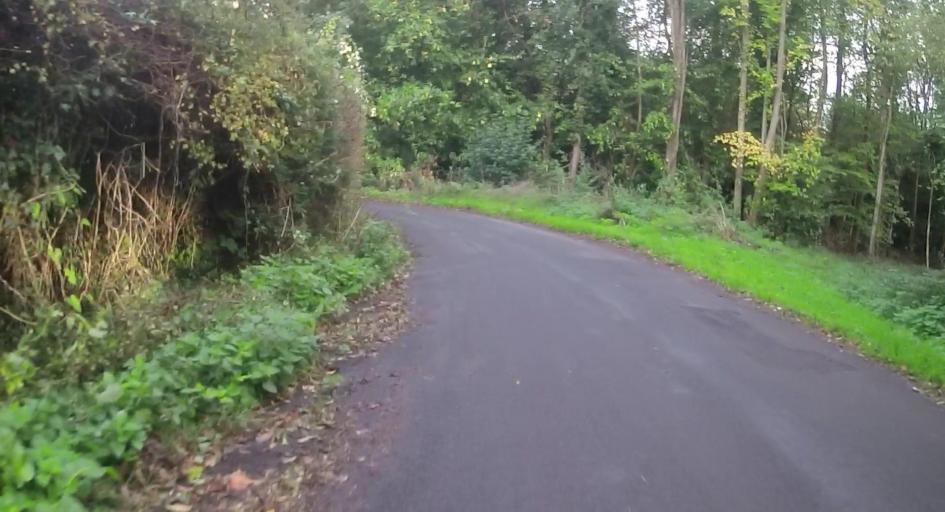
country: GB
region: England
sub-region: West Berkshire
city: Thatcham
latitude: 51.4070
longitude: -1.1905
